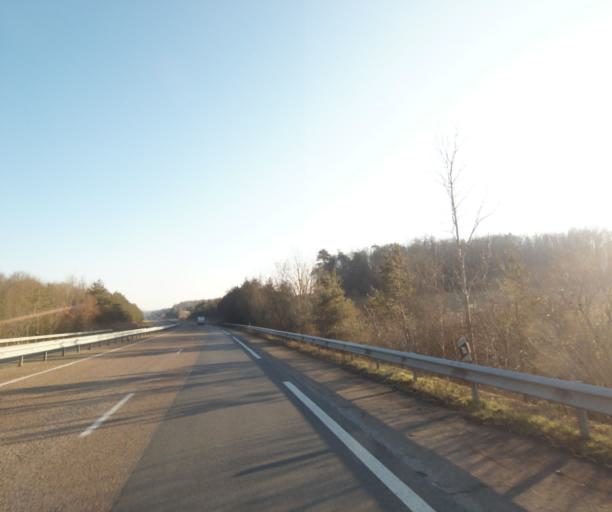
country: FR
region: Champagne-Ardenne
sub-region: Departement de la Haute-Marne
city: Chevillon
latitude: 48.5103
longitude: 5.0951
